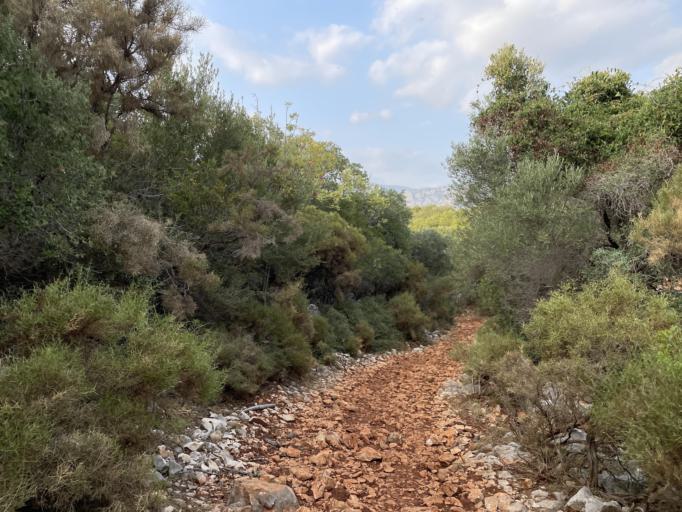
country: TR
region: Antalya
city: Kas
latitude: 36.1641
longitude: 29.6540
